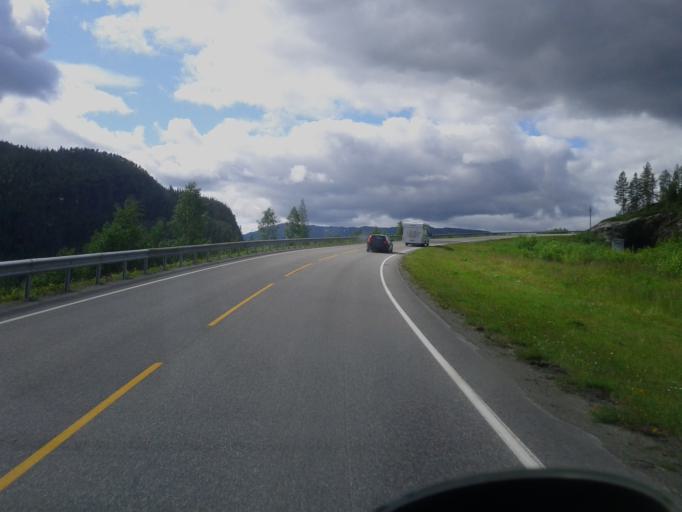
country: NO
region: Nord-Trondelag
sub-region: Grong
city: Grong
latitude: 64.5376
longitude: 12.4452
